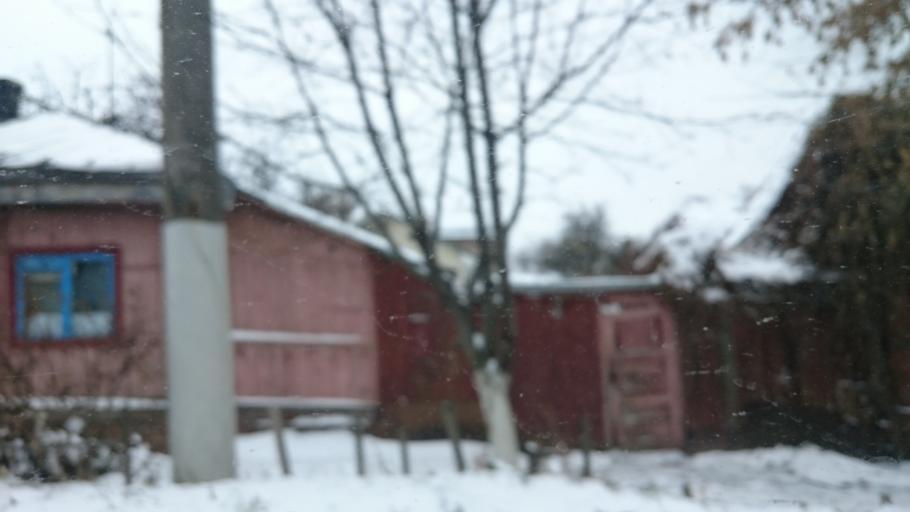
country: RU
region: Tula
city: Tula
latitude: 54.1980
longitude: 37.6335
